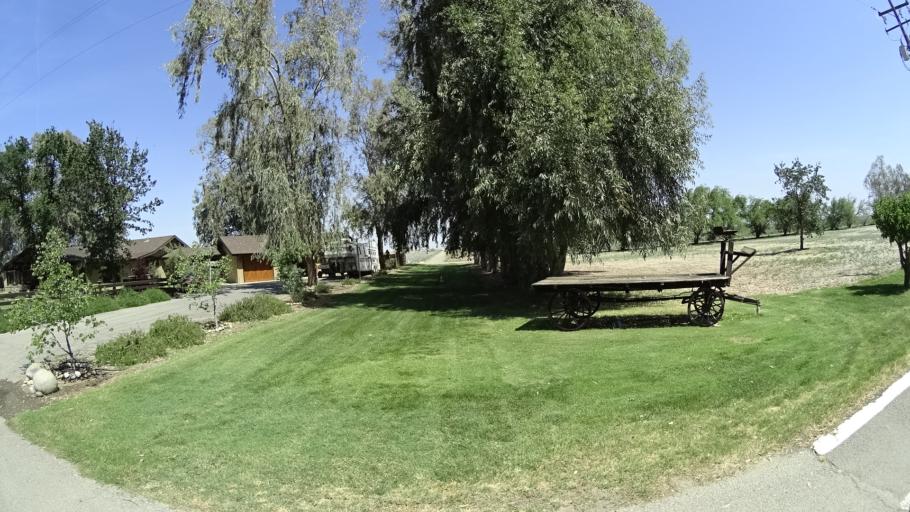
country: US
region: California
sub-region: Kings County
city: Stratford
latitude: 36.1233
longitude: -119.8873
